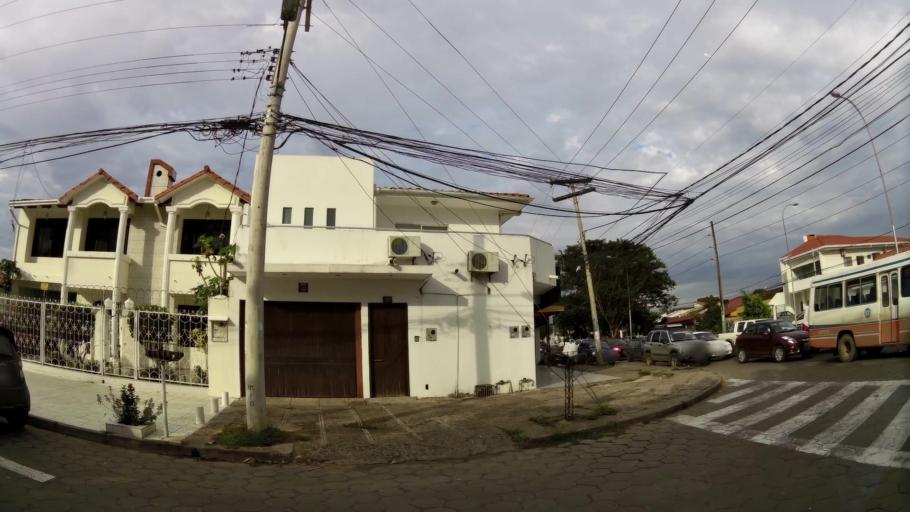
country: BO
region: Santa Cruz
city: Santa Cruz de la Sierra
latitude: -17.7519
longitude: -63.1698
